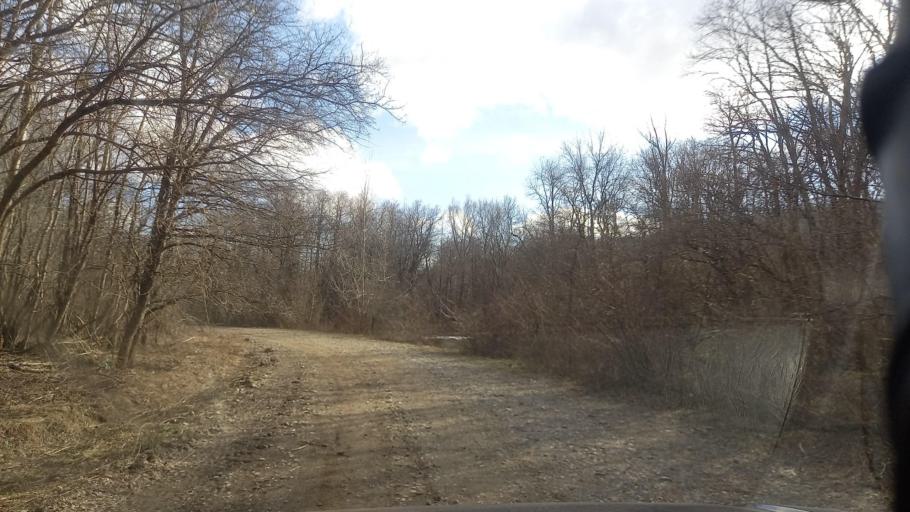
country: RU
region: Krasnodarskiy
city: Smolenskaya
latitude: 44.6210
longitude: 38.8243
